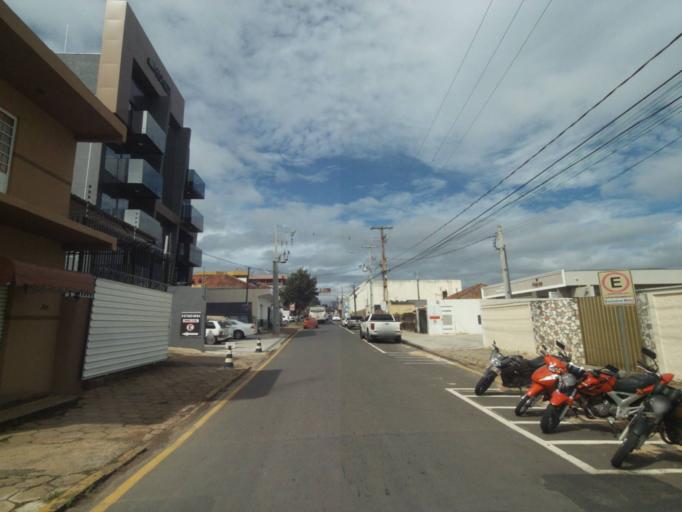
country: BR
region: Parana
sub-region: Telemaco Borba
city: Telemaco Borba
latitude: -24.3270
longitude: -50.6233
